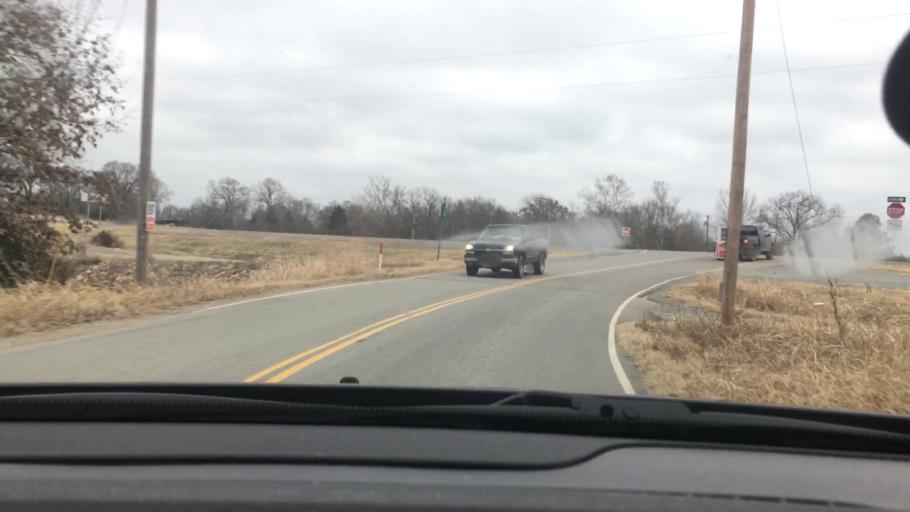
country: US
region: Oklahoma
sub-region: Atoka County
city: Atoka
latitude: 34.3443
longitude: -96.0754
